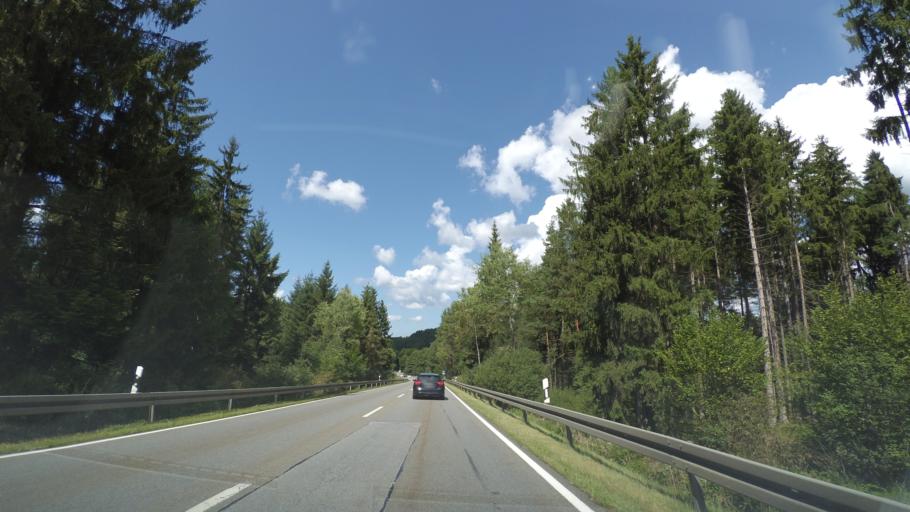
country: DE
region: Bavaria
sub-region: Lower Bavaria
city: Viechtach
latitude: 49.0502
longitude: 12.9252
